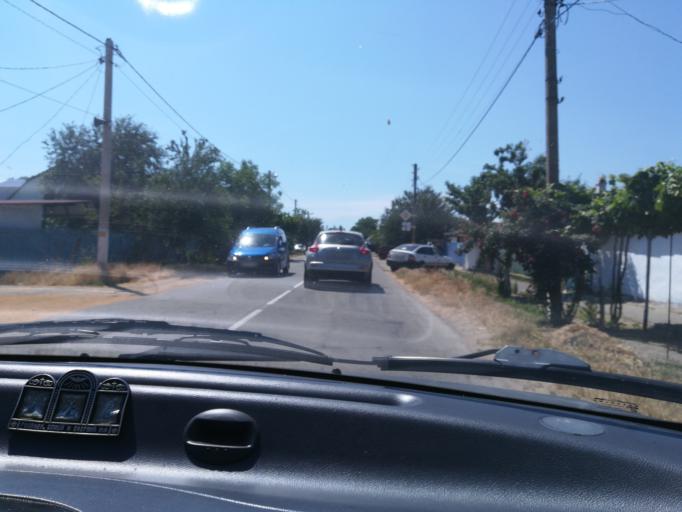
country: RU
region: Krasnodarskiy
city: Blagovetschenskaya
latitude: 45.0564
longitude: 37.1219
